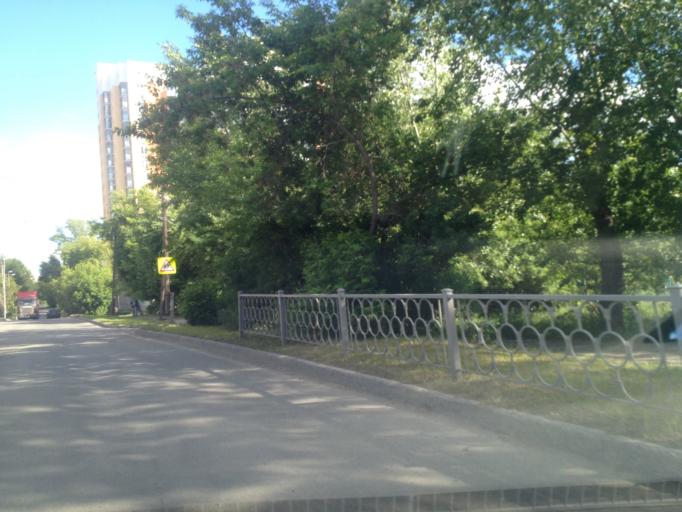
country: RU
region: Sverdlovsk
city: Yekaterinburg
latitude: 56.8631
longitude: 60.5753
